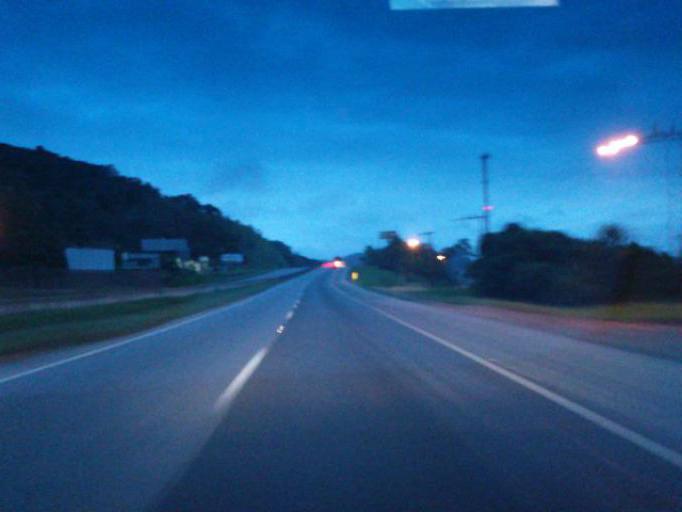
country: BR
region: Santa Catarina
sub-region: Penha
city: Penha
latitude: -26.8220
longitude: -48.6858
